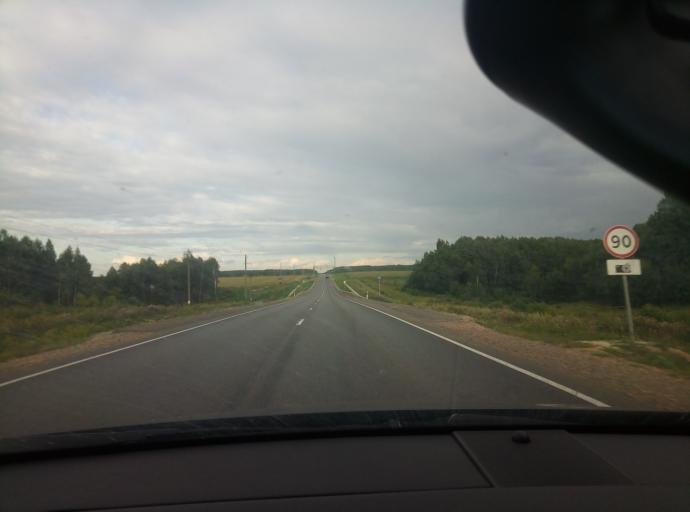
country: RU
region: Kaluga
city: Ferzikovo
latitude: 54.3681
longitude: 36.7008
